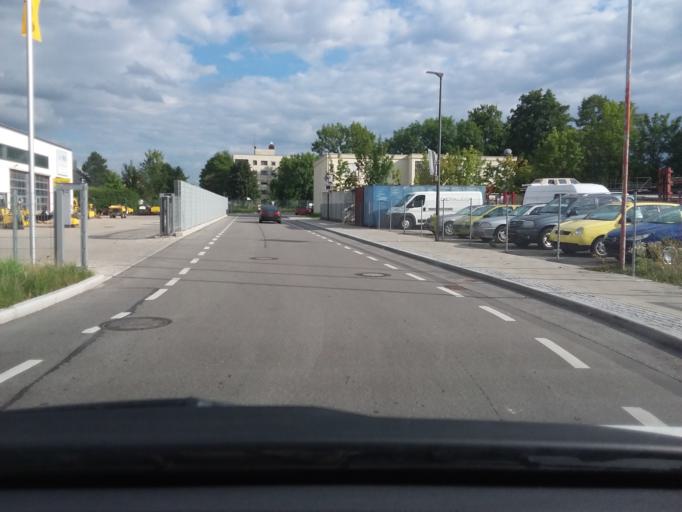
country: DE
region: Bavaria
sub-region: Upper Bavaria
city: Unterschleissheim
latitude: 48.2817
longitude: 11.5723
